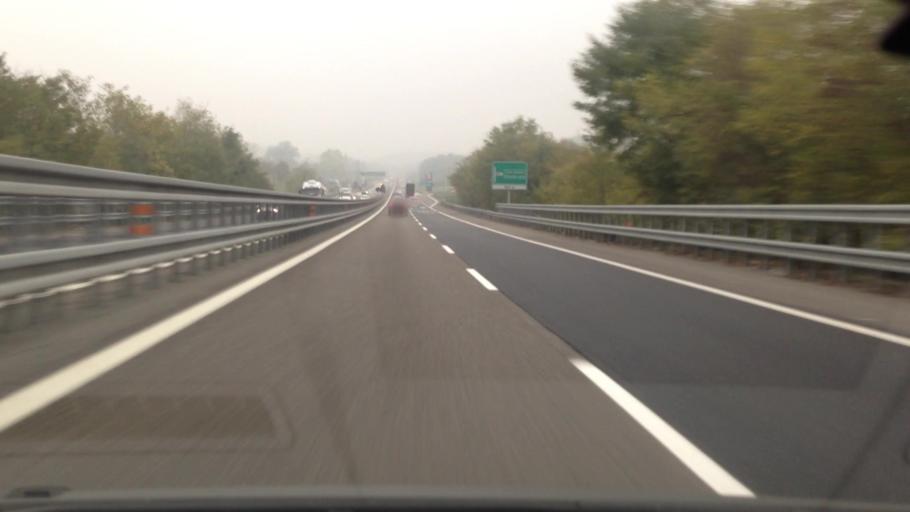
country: IT
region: Piedmont
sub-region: Provincia di Asti
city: Cerro Tanaro
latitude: 44.9046
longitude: 8.3700
